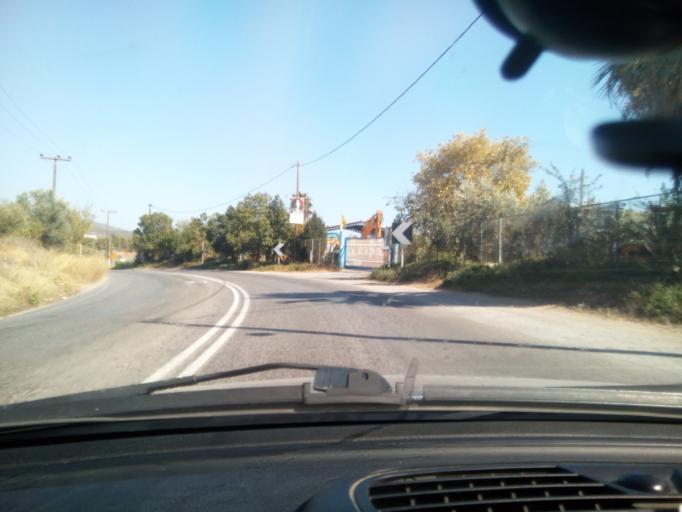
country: GR
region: Central Greece
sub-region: Nomos Evvoias
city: Vasilikon
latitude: 38.4177
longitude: 23.6874
